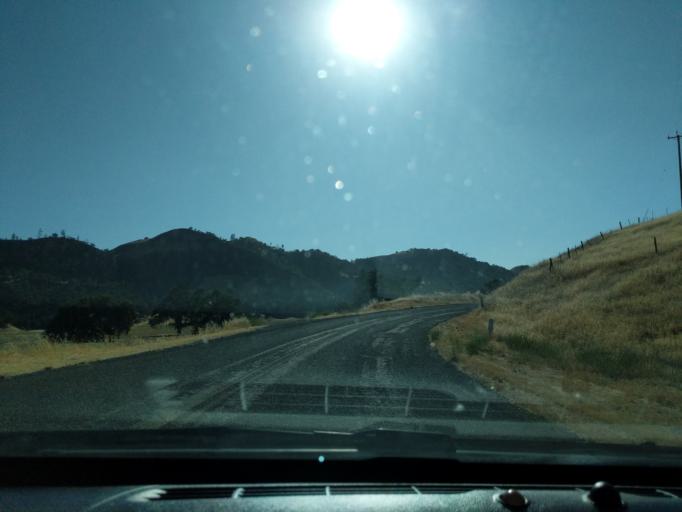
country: US
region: California
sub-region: Monterey County
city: King City
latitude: 36.1677
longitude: -120.7840
